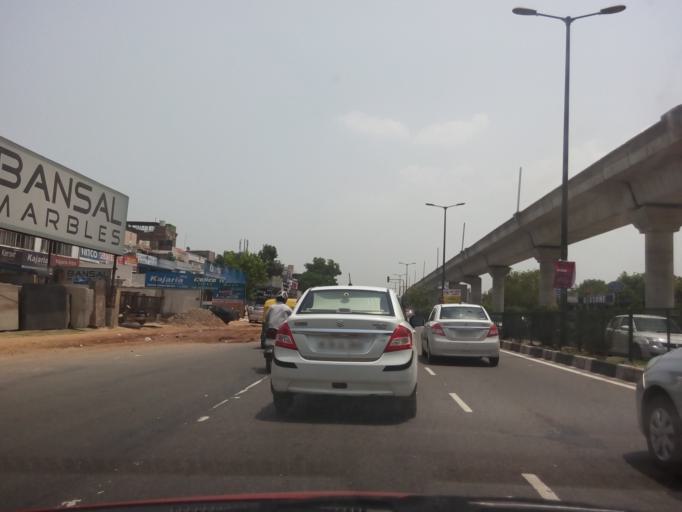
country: IN
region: NCT
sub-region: North West Delhi
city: Pitampura
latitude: 28.6448
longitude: 77.1272
